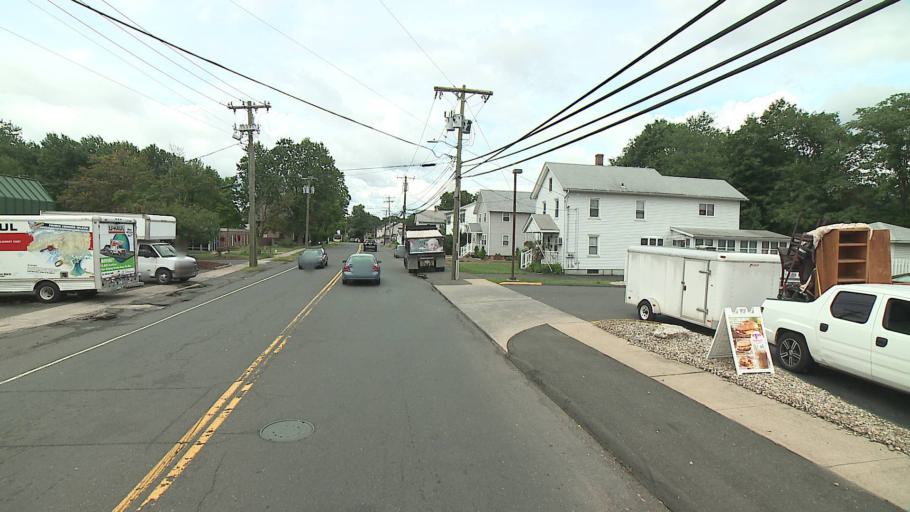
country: US
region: Connecticut
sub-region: Hartford County
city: Plainville
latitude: 41.6728
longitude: -72.8595
